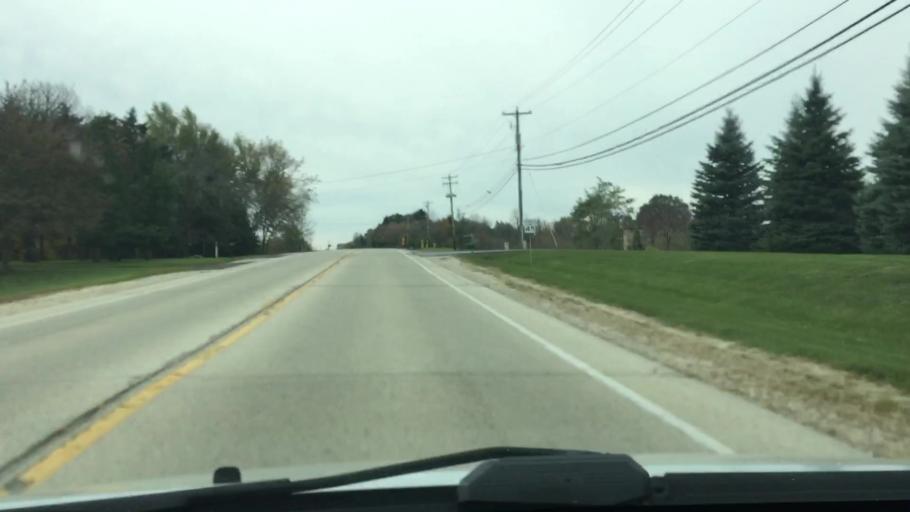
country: US
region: Wisconsin
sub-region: Waukesha County
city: Muskego
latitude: 42.9385
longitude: -88.1701
